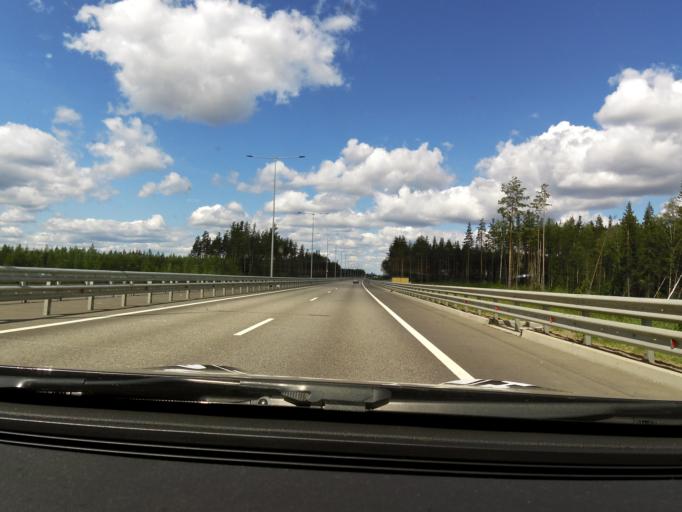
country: RU
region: Tverskaya
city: Krasnomayskiy
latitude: 57.4743
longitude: 34.3435
